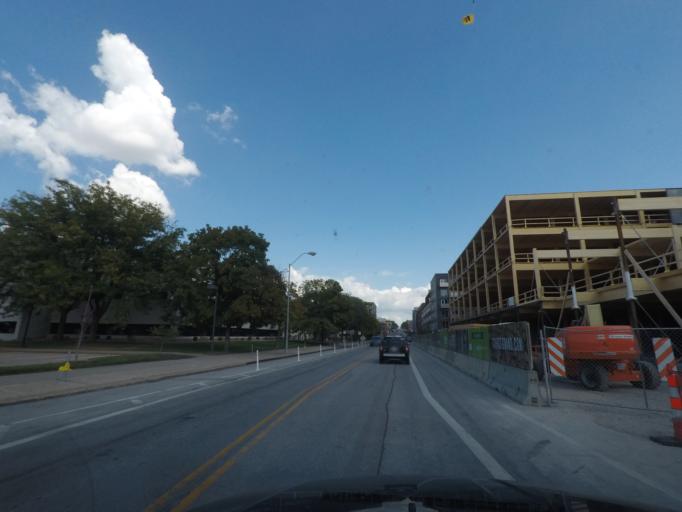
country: US
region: Iowa
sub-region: Polk County
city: Des Moines
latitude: 41.5898
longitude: -93.6160
